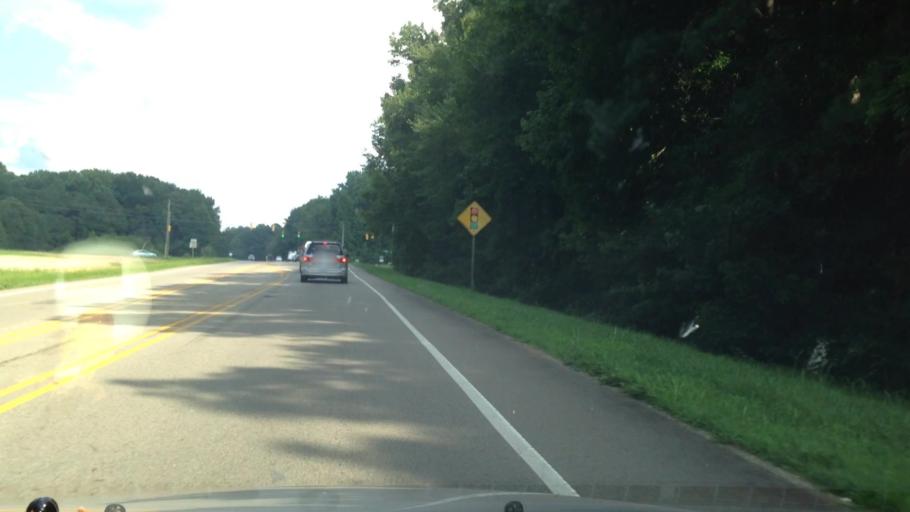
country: US
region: North Carolina
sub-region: Lee County
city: Broadway
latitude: 35.4414
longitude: -79.1009
